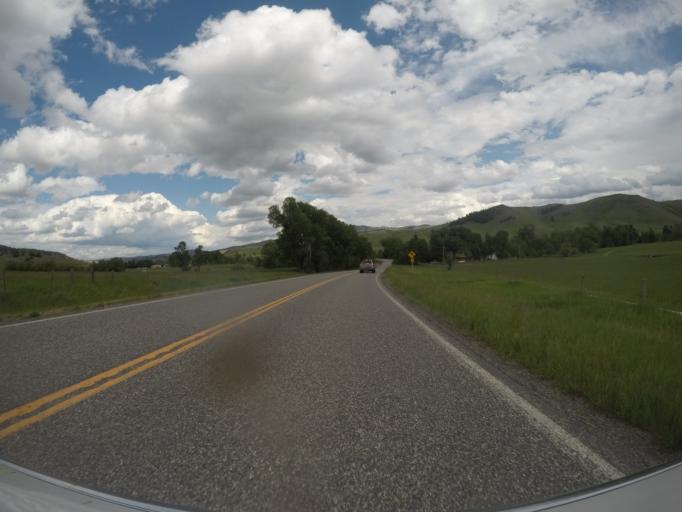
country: US
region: Montana
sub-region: Sweet Grass County
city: Big Timber
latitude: 45.6900
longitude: -110.0675
